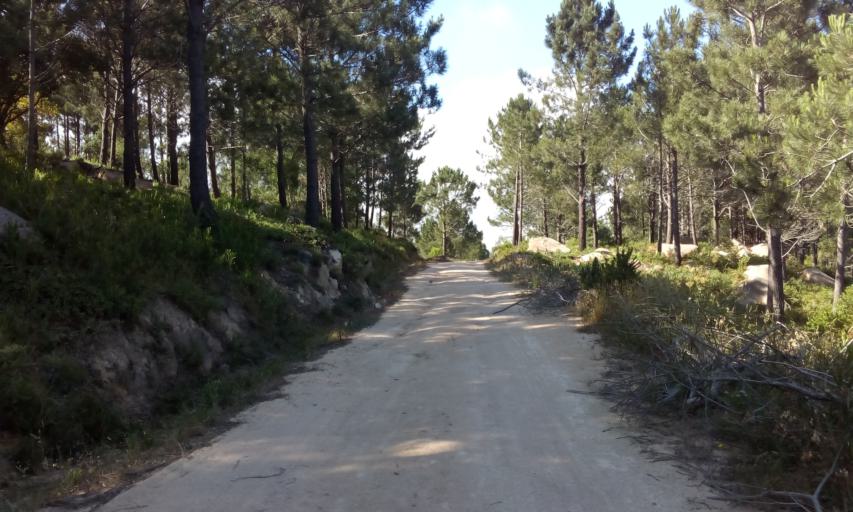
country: PT
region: Lisbon
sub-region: Cascais
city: Alcabideche
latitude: 38.7613
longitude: -9.4310
